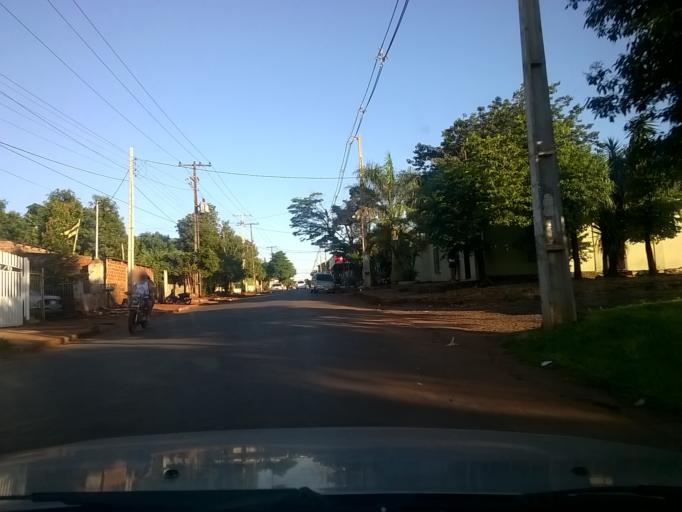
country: PY
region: Alto Parana
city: Presidente Franco
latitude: -25.5348
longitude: -54.6441
